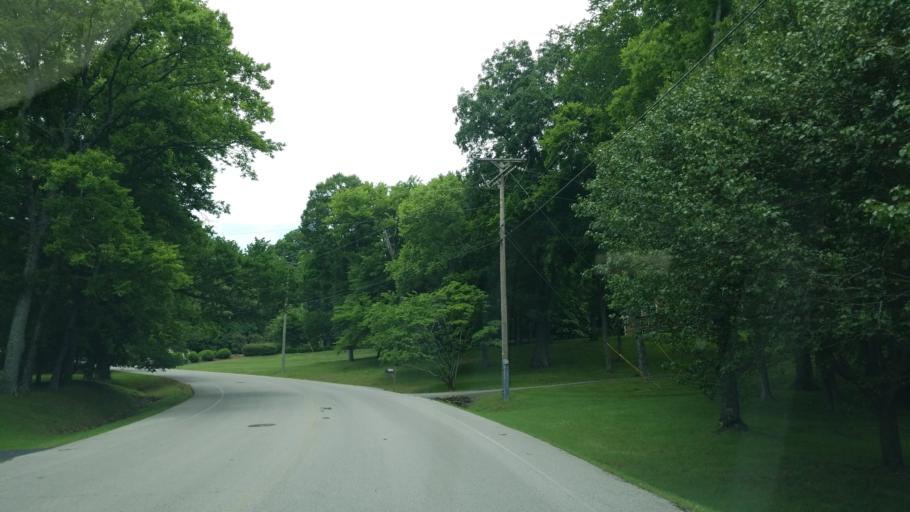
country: US
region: Tennessee
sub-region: Williamson County
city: Brentwood
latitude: 36.0394
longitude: -86.7907
